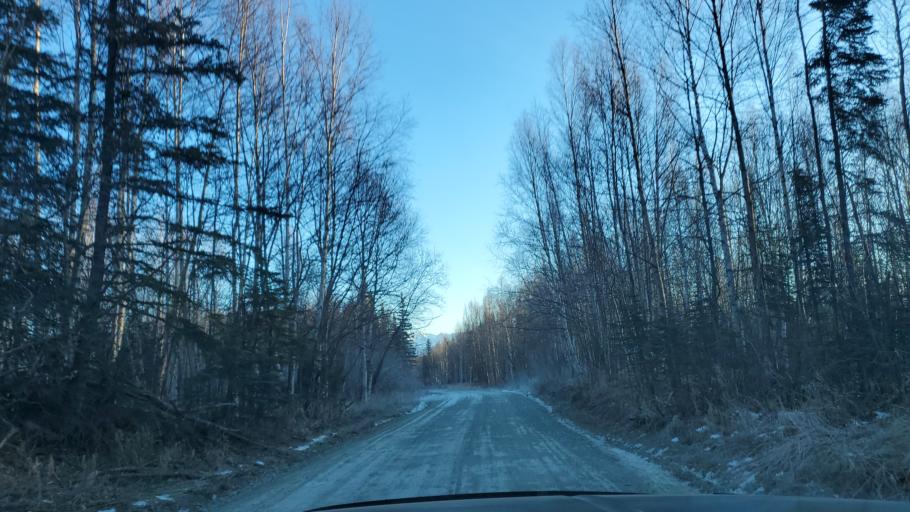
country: US
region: Alaska
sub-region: Matanuska-Susitna Borough
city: Tanaina
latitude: 61.6428
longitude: -149.3648
